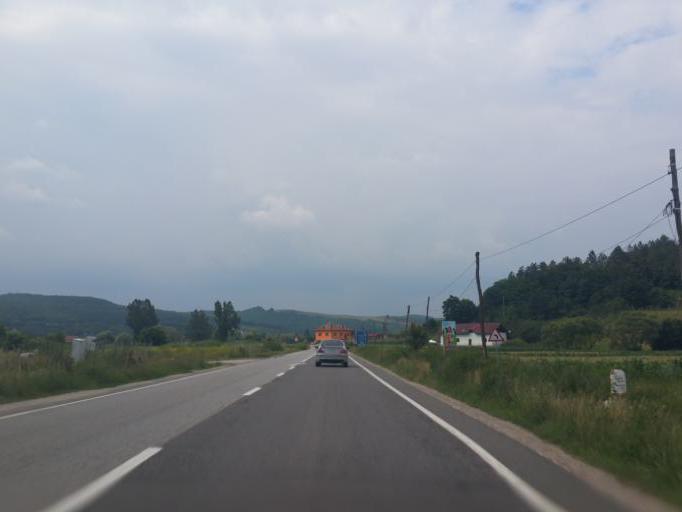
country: RO
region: Salaj
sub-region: Comuna Romanasi
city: Romanasi
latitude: 47.1049
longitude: 23.1863
